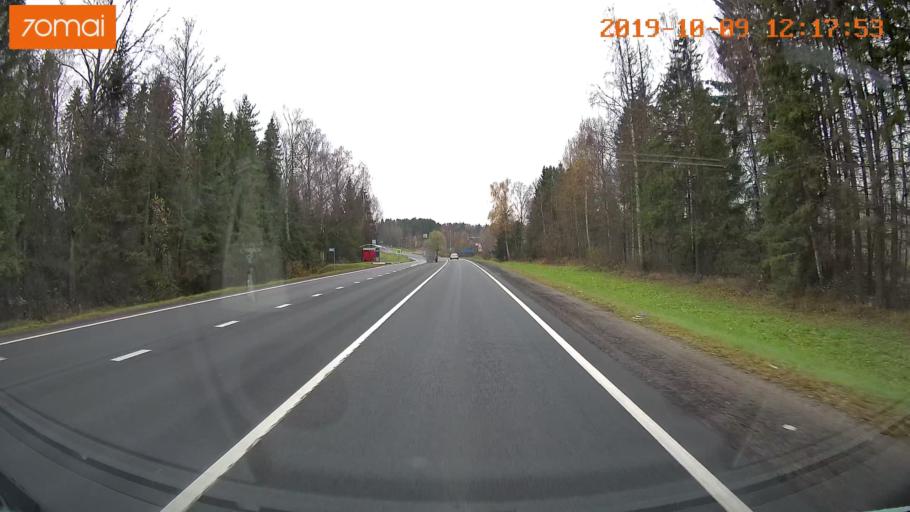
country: RU
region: Jaroslavl
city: Prechistoye
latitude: 58.4503
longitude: 40.3212
